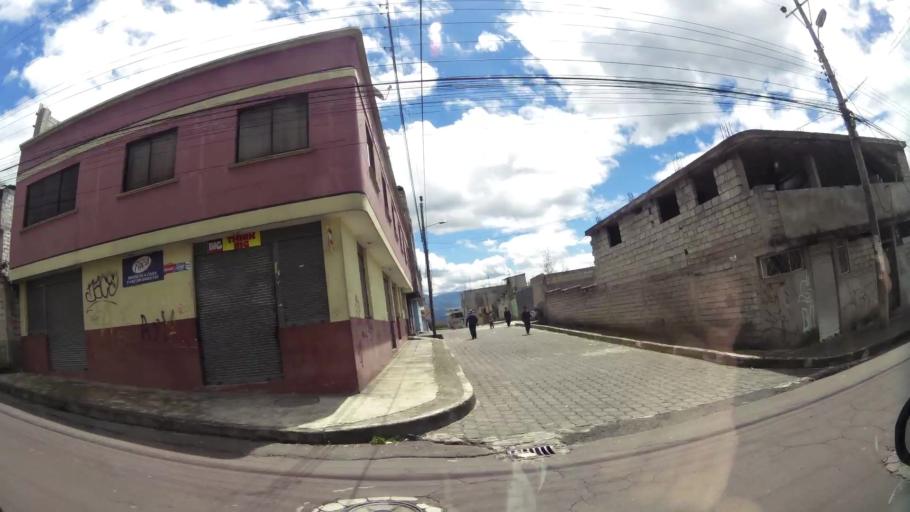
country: EC
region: Pichincha
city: Sangolqui
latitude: -0.3435
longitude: -78.5606
